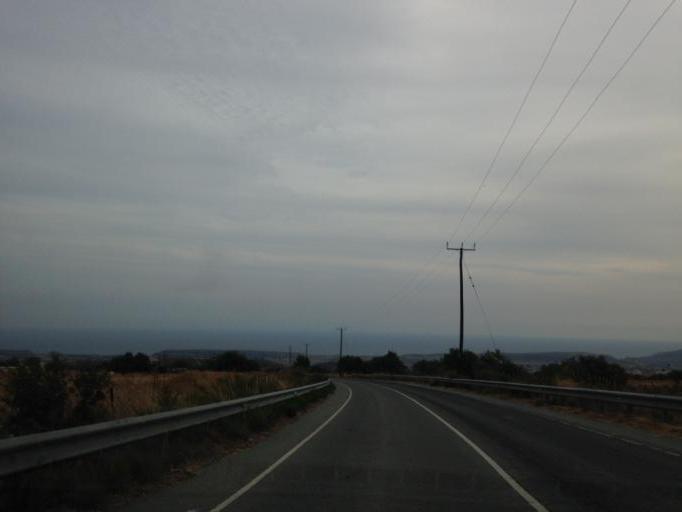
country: CY
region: Limassol
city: Pachna
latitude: 34.7318
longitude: 32.7719
